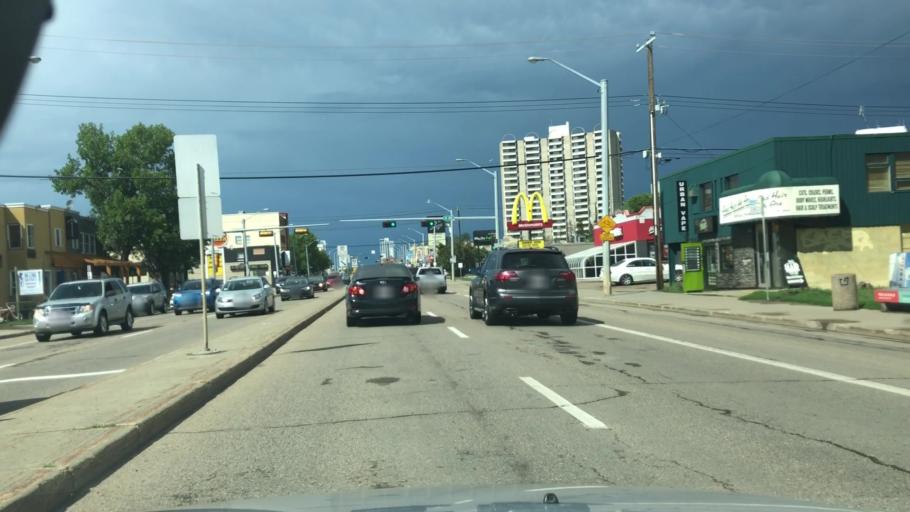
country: CA
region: Alberta
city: Edmonton
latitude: 53.5202
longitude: -113.5120
